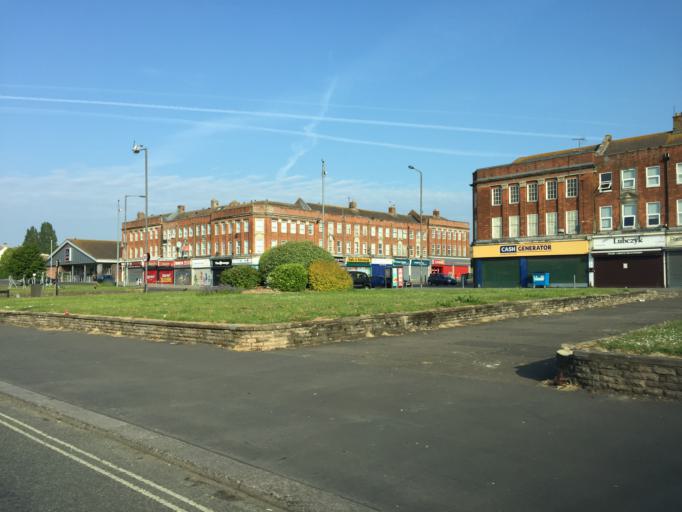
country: GB
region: England
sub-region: Bristol
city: Bristol
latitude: 51.5035
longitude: -2.6018
